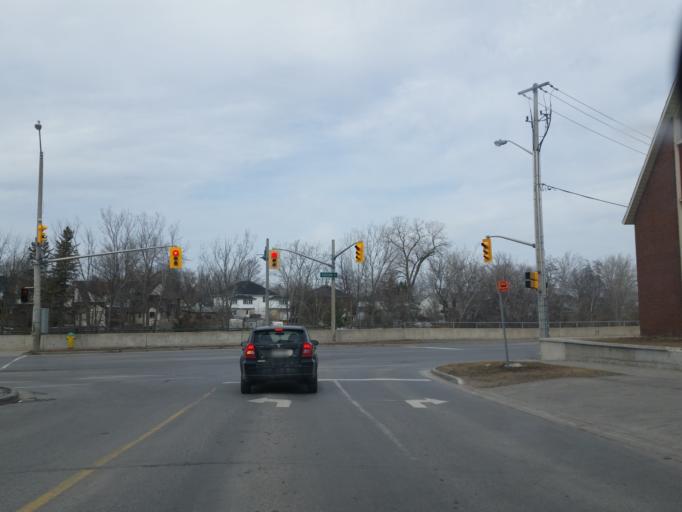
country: CA
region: Ontario
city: Belleville
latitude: 44.1702
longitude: -77.3838
